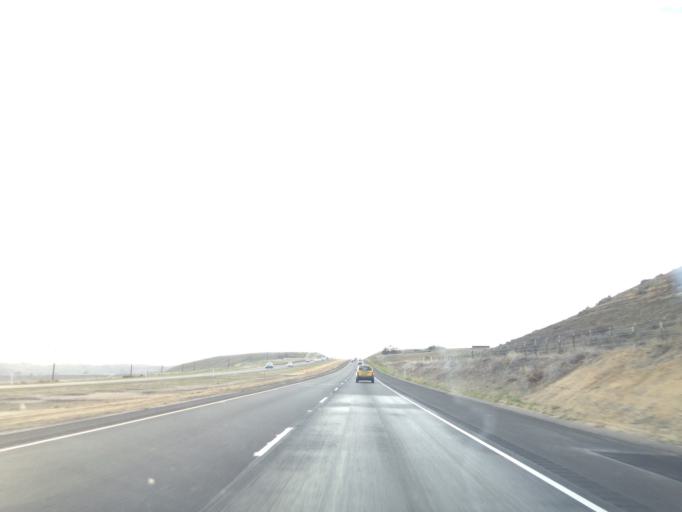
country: US
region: California
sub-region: San Luis Obispo County
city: Shandon
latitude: 35.6598
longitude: -120.4676
